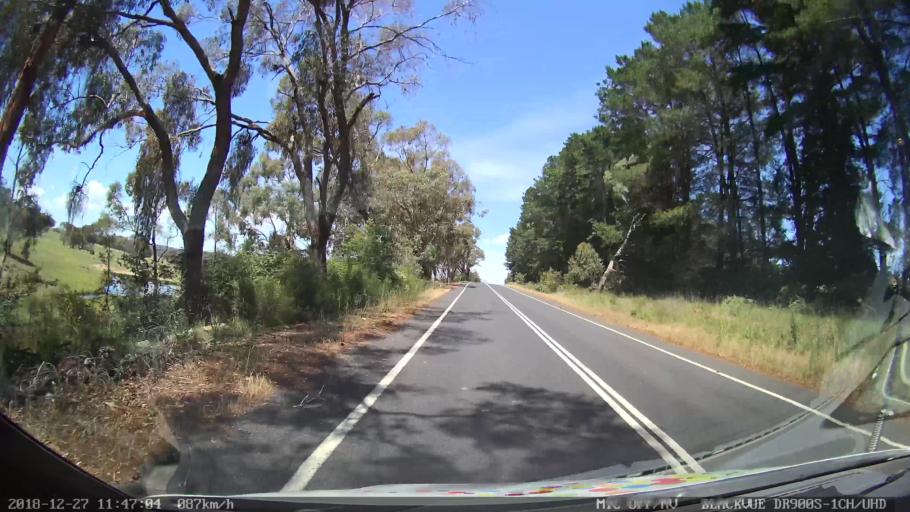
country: AU
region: New South Wales
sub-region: Bathurst Regional
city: Perthville
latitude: -33.5926
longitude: 149.4490
